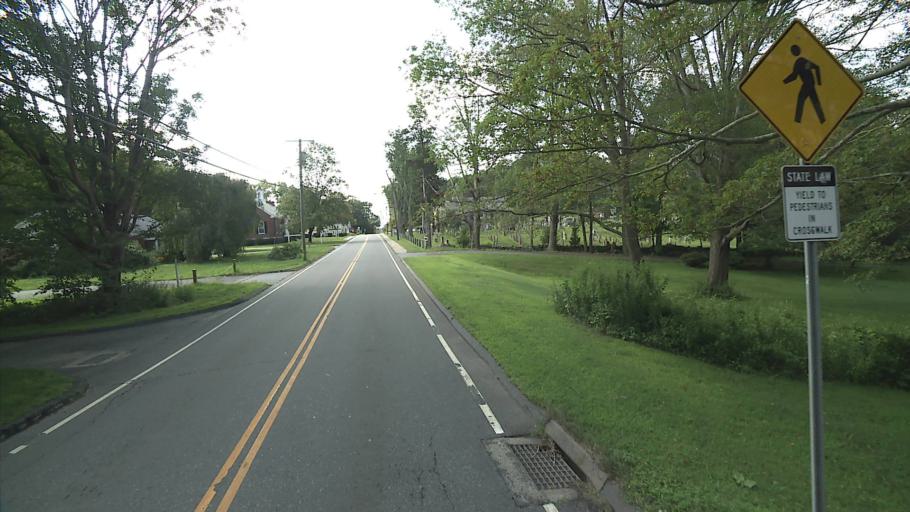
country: US
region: Connecticut
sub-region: Middlesex County
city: East Haddam
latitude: 41.4565
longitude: -72.4627
